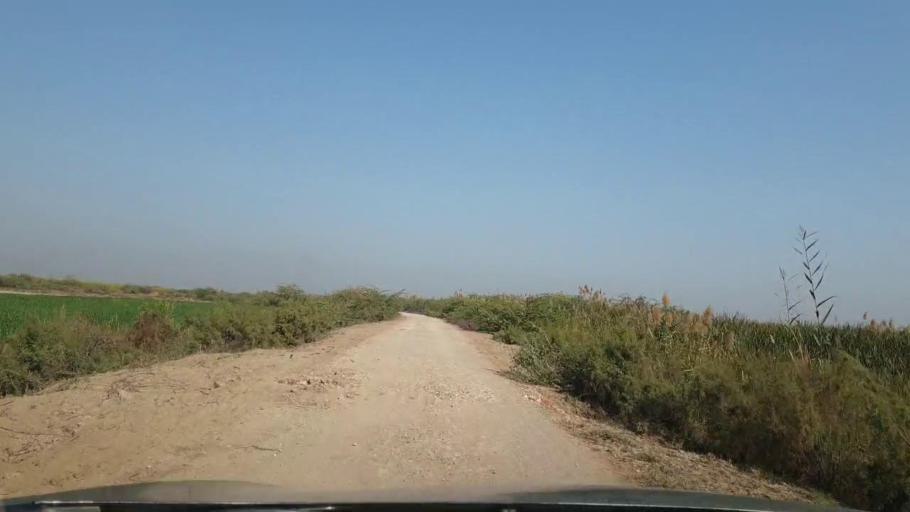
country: PK
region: Sindh
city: Mirpur Khas
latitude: 25.6539
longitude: 68.9133
